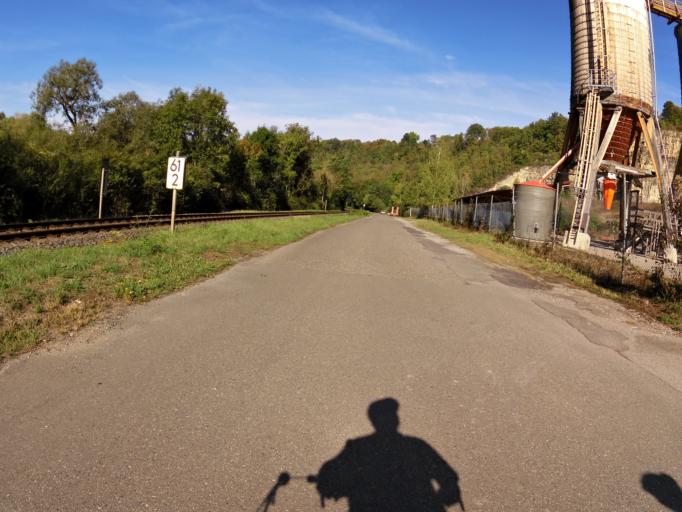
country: DE
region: Baden-Wuerttemberg
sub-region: Tuebingen Region
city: Rottenburg
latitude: 48.4679
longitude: 8.9134
